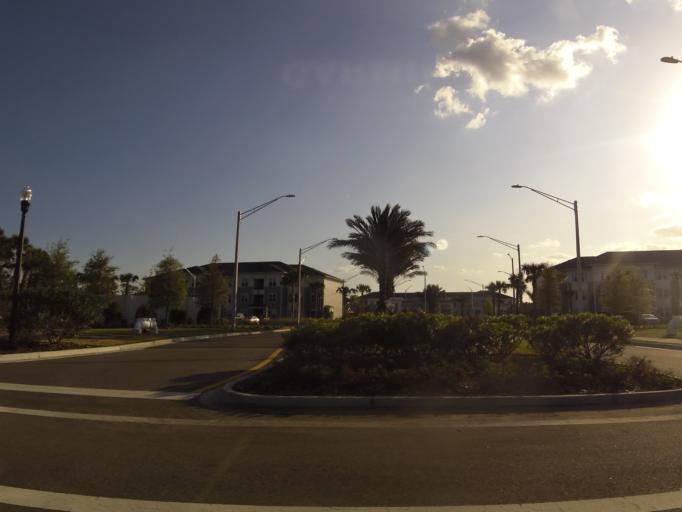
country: US
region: Florida
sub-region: Saint Johns County
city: Palm Valley
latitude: 30.0774
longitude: -81.4849
